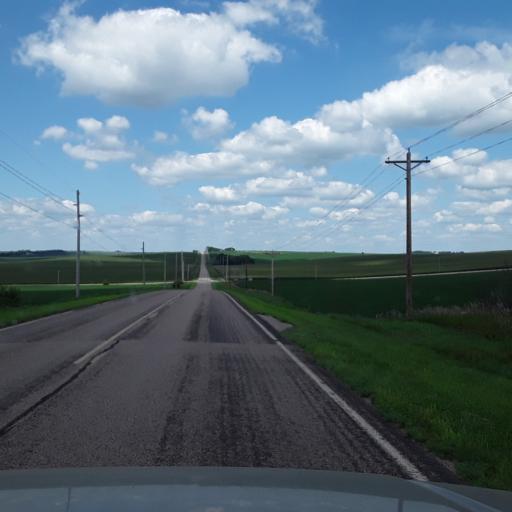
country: US
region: Nebraska
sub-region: Nance County
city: Genoa
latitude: 41.5373
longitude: -97.6959
